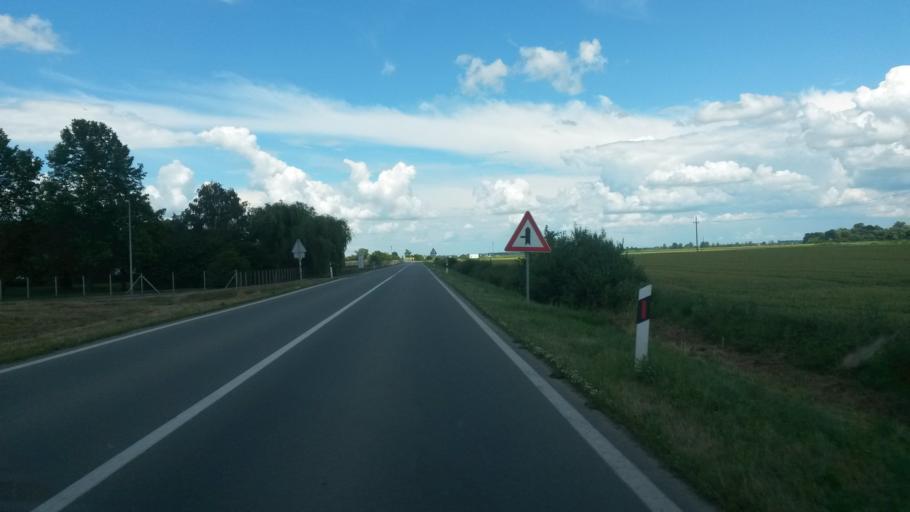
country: HR
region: Osjecko-Baranjska
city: Vuka
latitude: 45.4657
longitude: 18.5235
